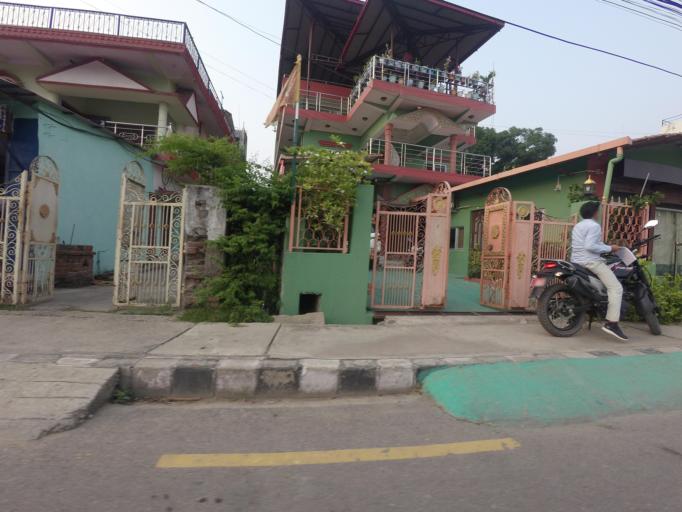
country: NP
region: Western Region
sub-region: Lumbini Zone
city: Bhairahawa
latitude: 27.5151
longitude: 83.4516
